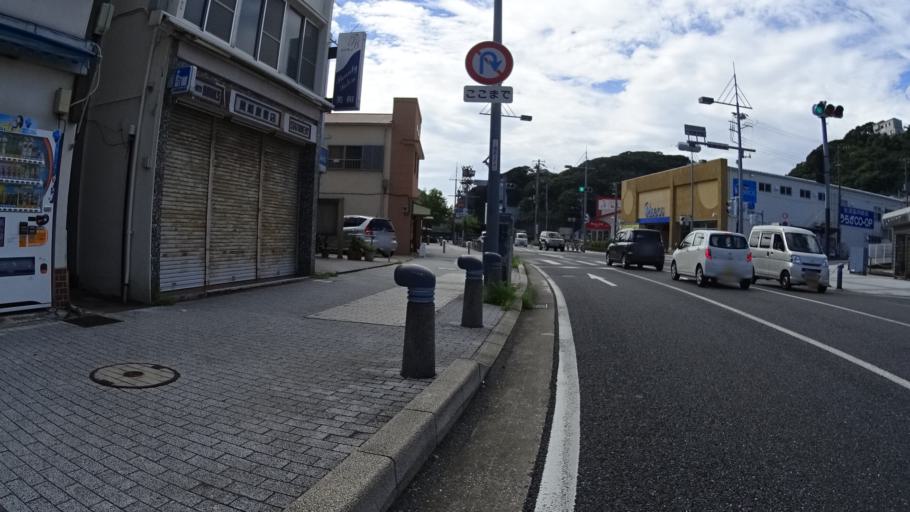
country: JP
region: Kanagawa
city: Yokosuka
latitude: 35.2467
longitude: 139.7150
